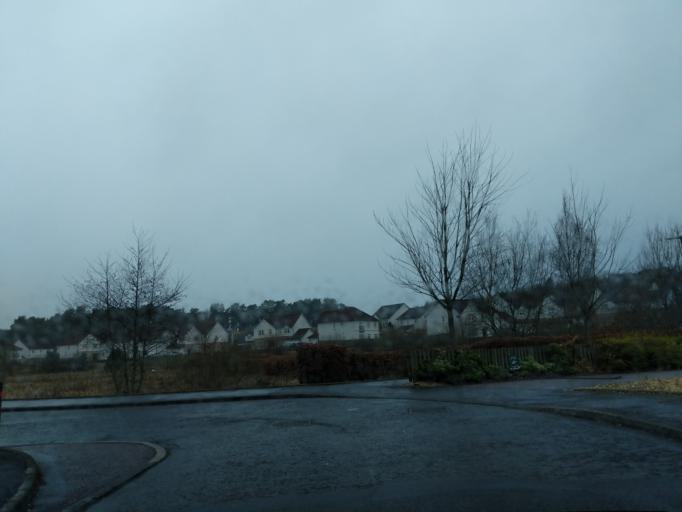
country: GB
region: Scotland
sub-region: Falkirk
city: Falkirk
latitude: 55.9845
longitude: -3.7942
